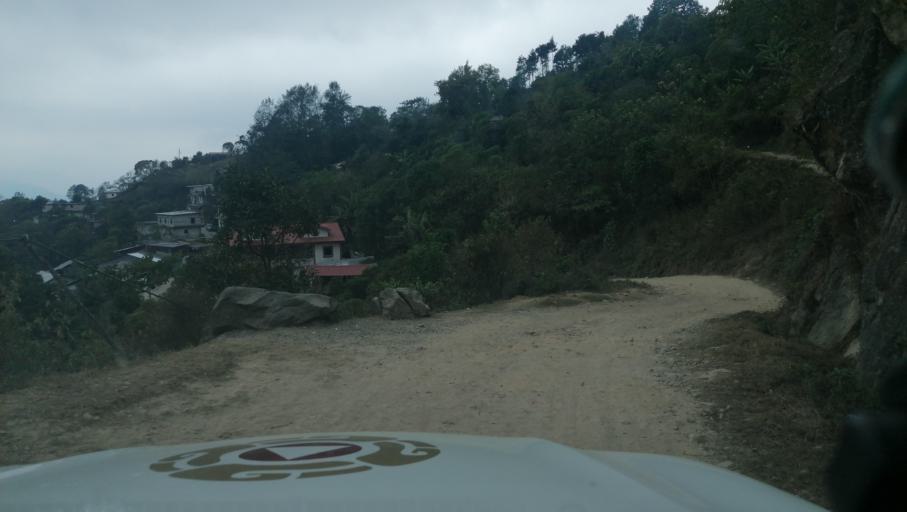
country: GT
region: San Marcos
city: Tacana
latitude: 15.2054
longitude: -92.1773
